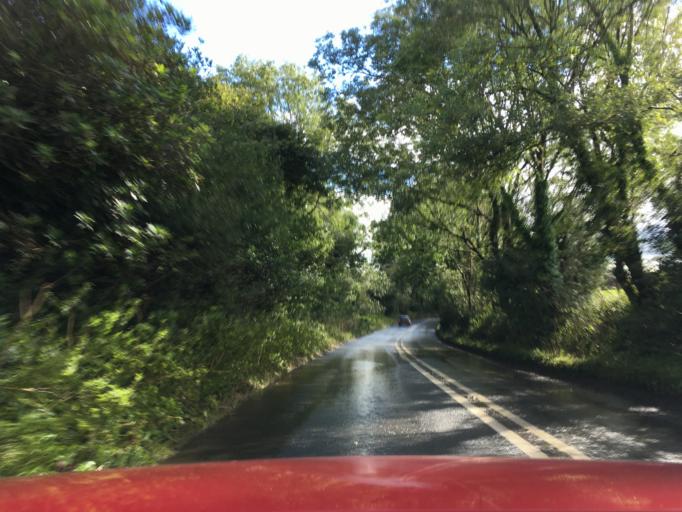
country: GB
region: England
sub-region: Devon
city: Kingsbridge
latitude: 50.3368
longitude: -3.7422
